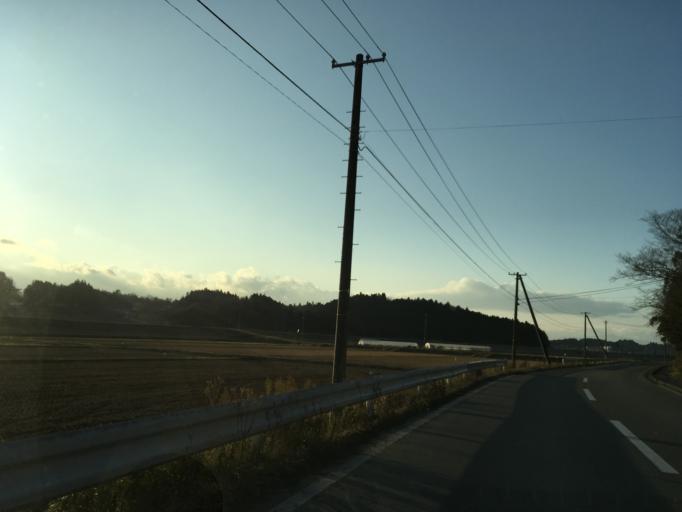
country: JP
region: Iwate
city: Ichinoseki
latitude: 38.8083
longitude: 141.2171
